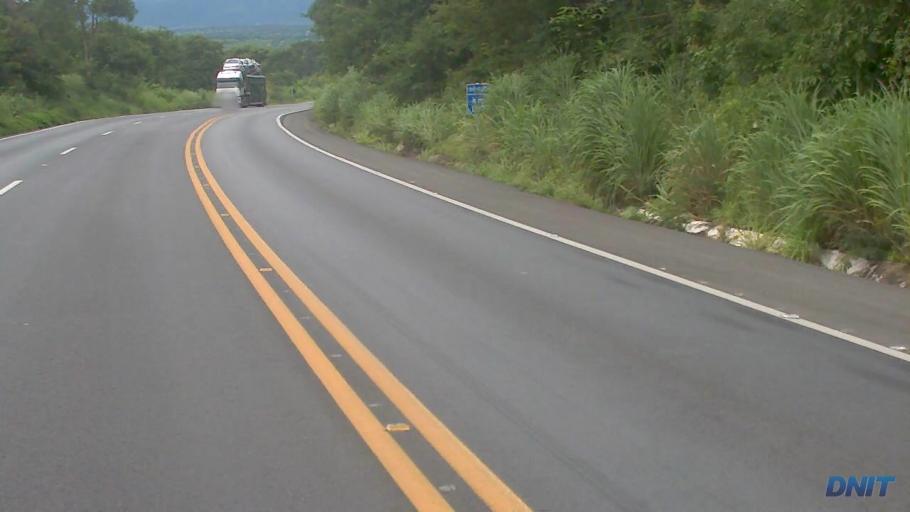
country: BR
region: Goias
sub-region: Posse
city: Posse
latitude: -14.3612
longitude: -46.4453
